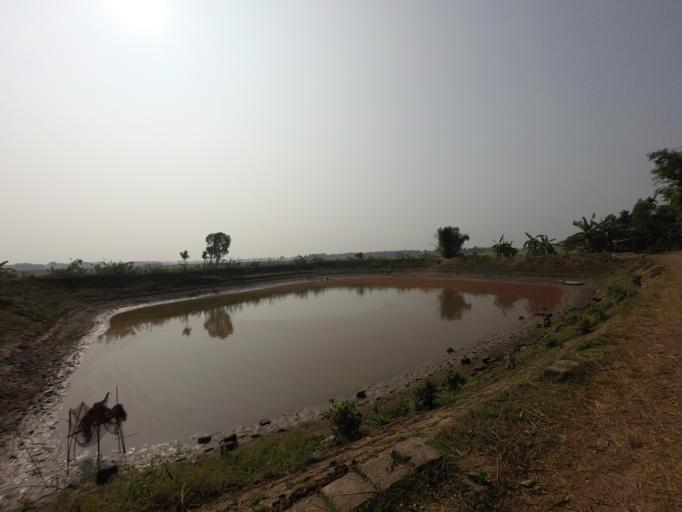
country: BD
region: Dhaka
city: Netrakona
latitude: 25.0124
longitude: 90.6722
